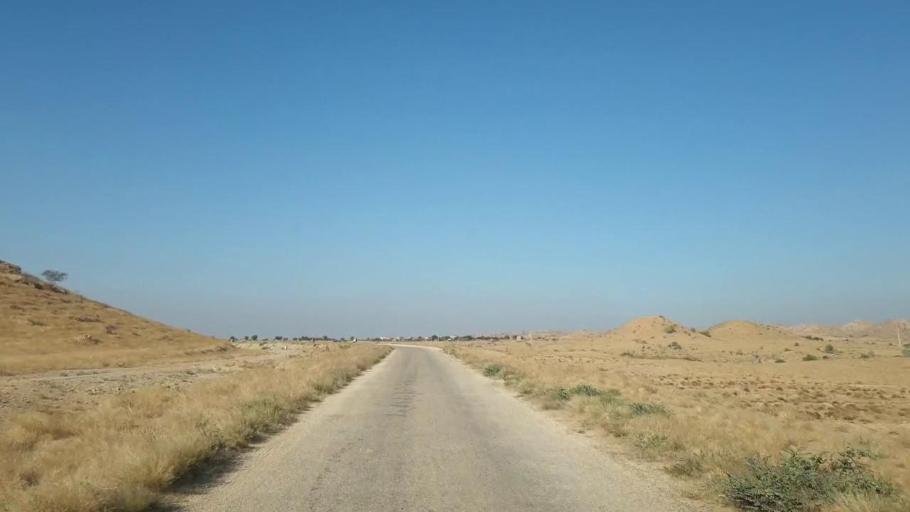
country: PK
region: Sindh
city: Malir Cantonment
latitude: 25.4154
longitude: 67.4640
